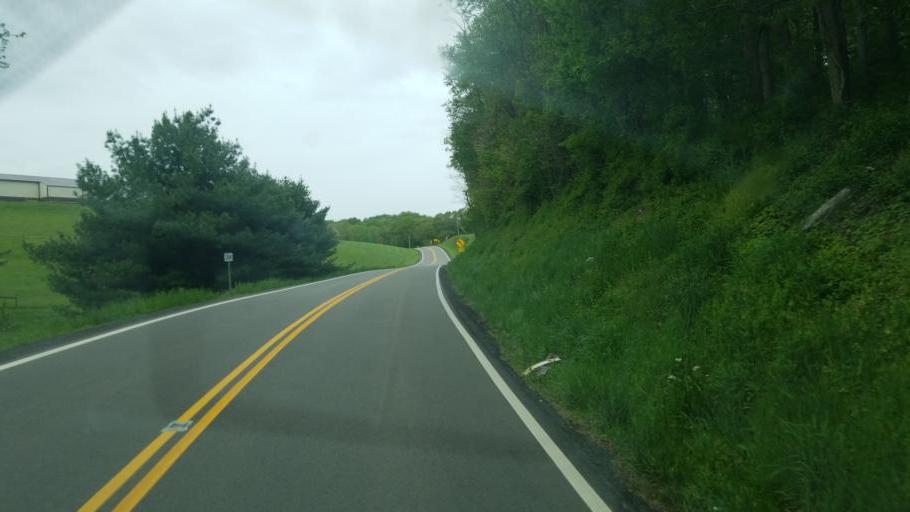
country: US
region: Ohio
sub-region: Coshocton County
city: Coshocton
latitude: 40.2385
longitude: -81.8160
